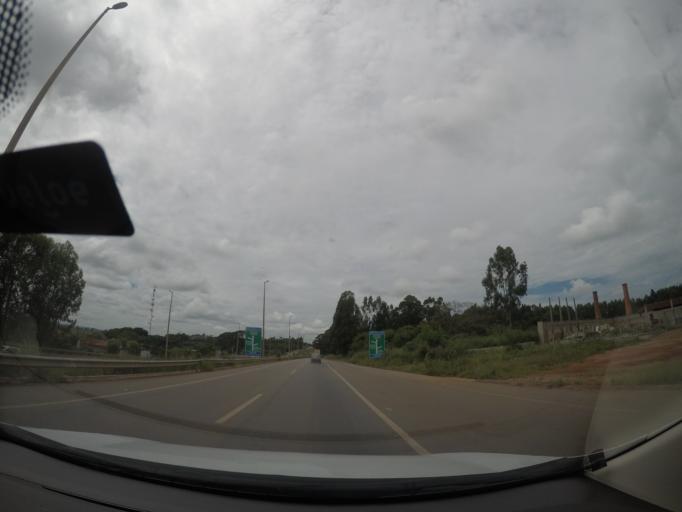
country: BR
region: Goias
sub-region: Inhumas
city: Inhumas
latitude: -16.3875
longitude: -49.4968
